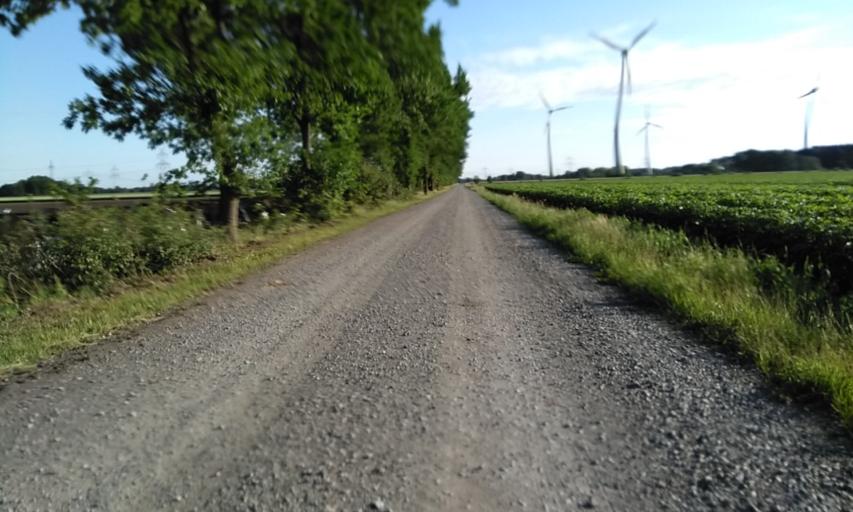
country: DE
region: Lower Saxony
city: Deinste
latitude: 53.5128
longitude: 9.4593
